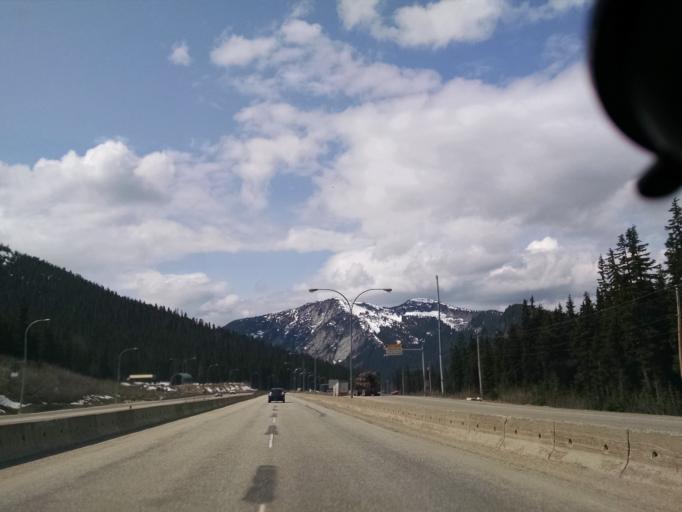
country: CA
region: British Columbia
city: Hope
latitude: 49.5955
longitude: -121.1151
